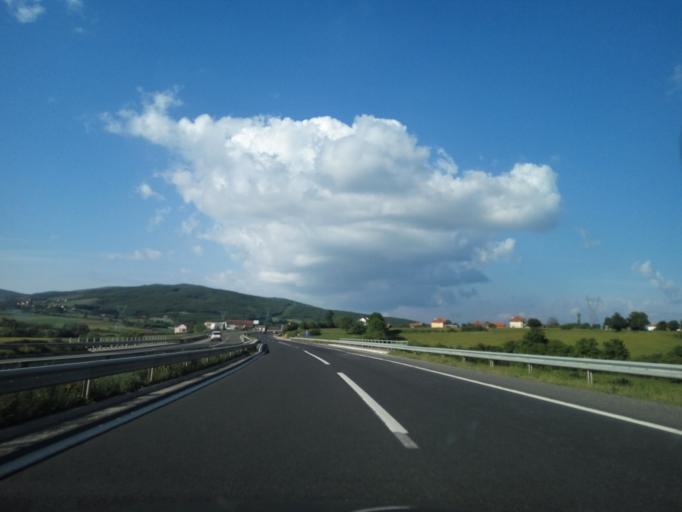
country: XK
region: Prizren
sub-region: Komuna e Malisheves
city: Llazice
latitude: 42.5612
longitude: 20.8261
